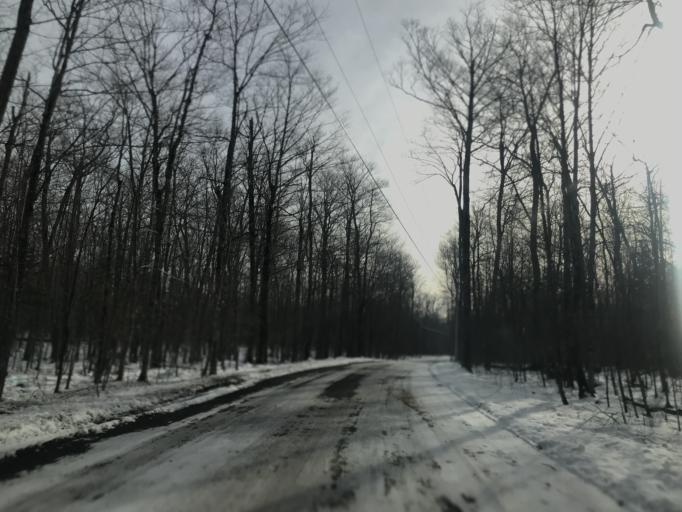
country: US
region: Wisconsin
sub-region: Door County
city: Sturgeon Bay
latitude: 45.1476
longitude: -87.0538
